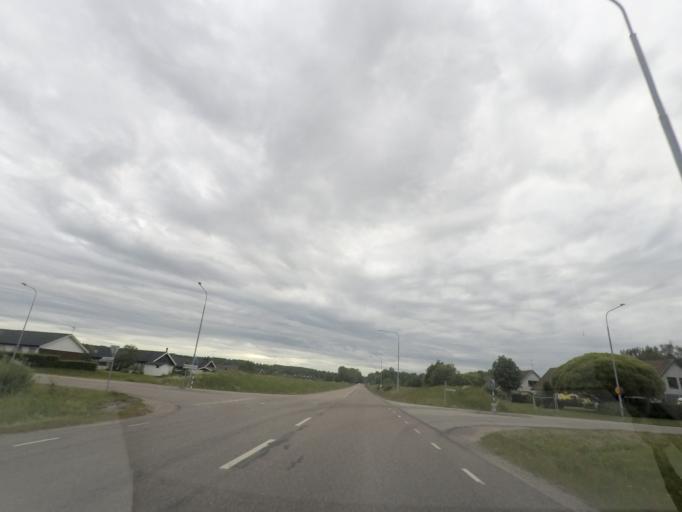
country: SE
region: Vaestmanland
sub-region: Arboga Kommun
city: Arboga
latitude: 59.4043
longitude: 15.8229
